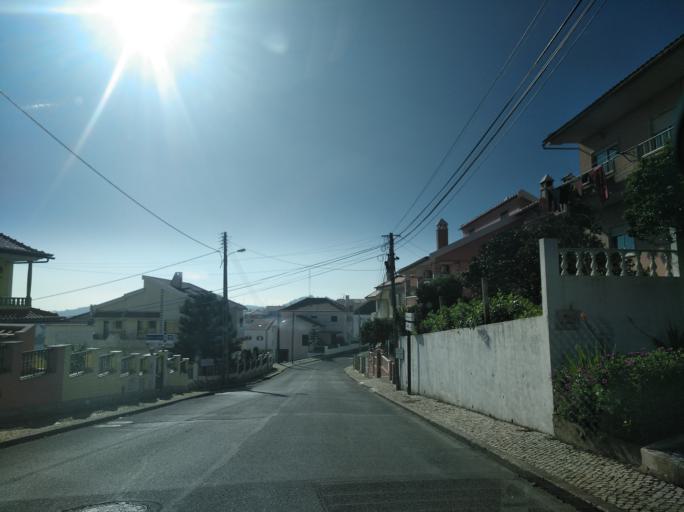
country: PT
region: Lisbon
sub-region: Odivelas
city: Famoes
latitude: 38.8006
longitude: -9.2181
